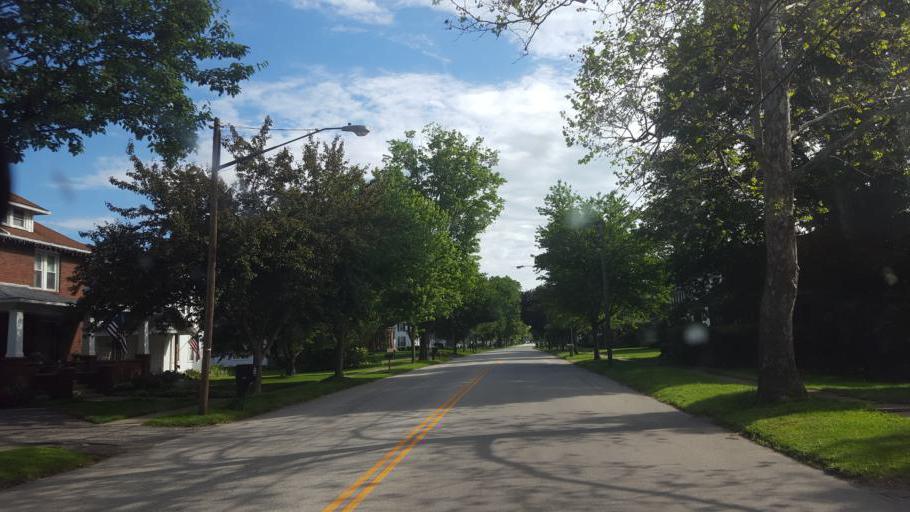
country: US
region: Ohio
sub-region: Wayne County
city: Creston
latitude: 40.9874
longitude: -81.8932
